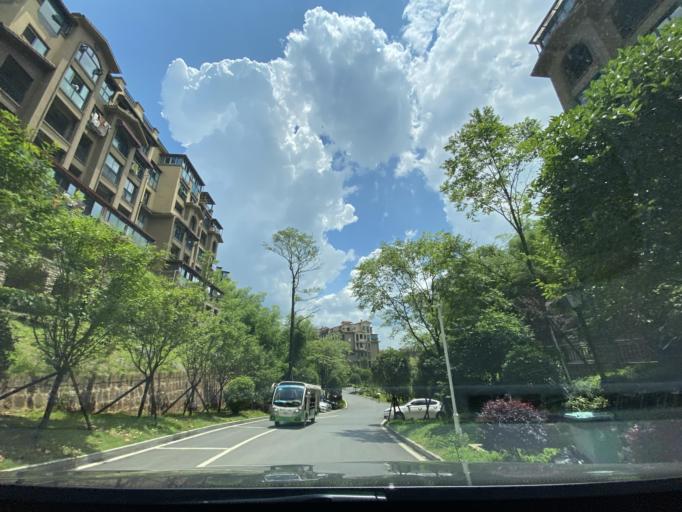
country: CN
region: Guizhou Sheng
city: Changqi
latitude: 28.5364
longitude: 105.9747
